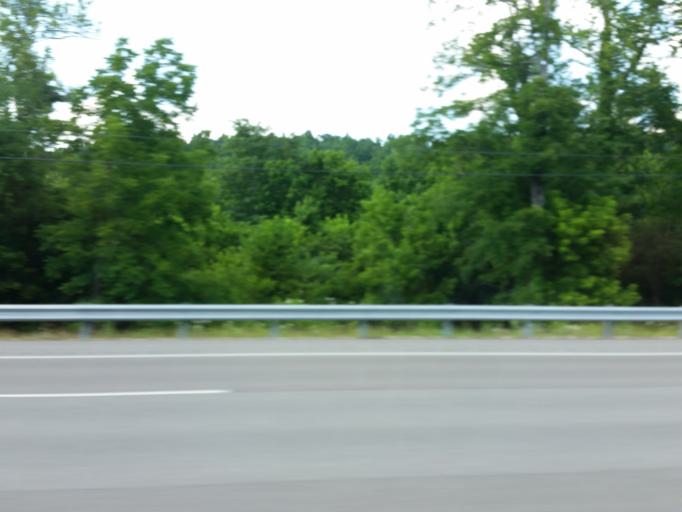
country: US
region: Tennessee
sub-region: Lewis County
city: Hohenwald
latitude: 35.5671
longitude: -87.4120
